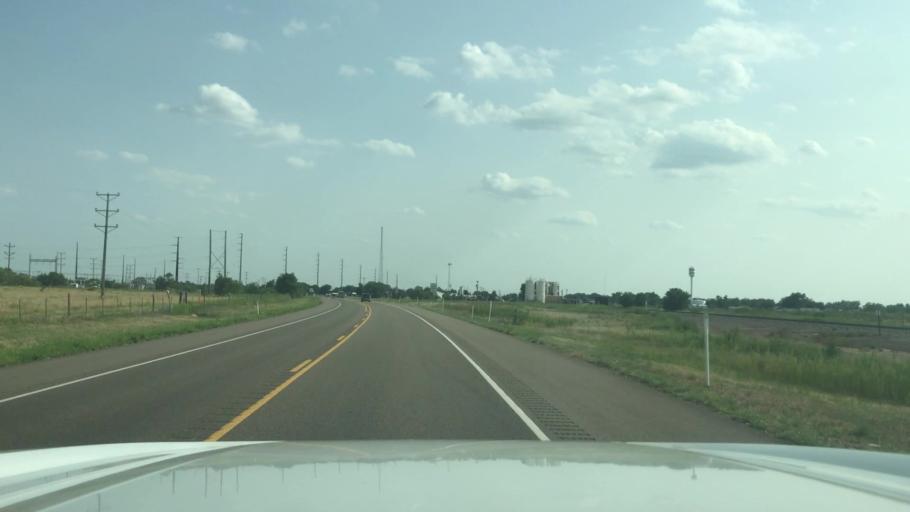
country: US
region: Texas
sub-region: Hartley County
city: Channing
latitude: 35.6944
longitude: -102.3282
